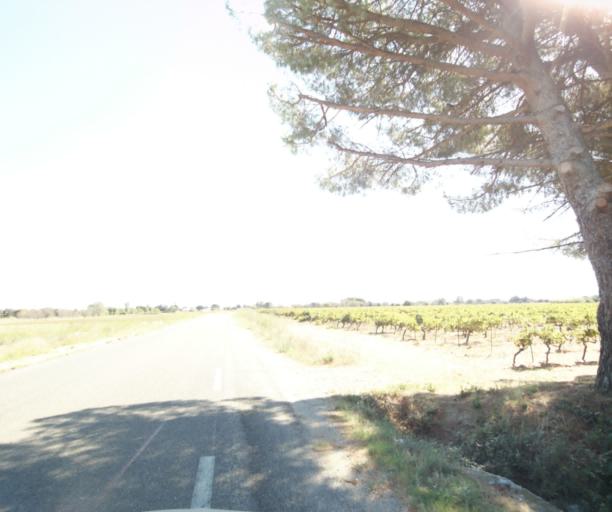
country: FR
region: Languedoc-Roussillon
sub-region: Departement du Gard
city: Manduel
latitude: 43.8119
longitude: 4.4530
